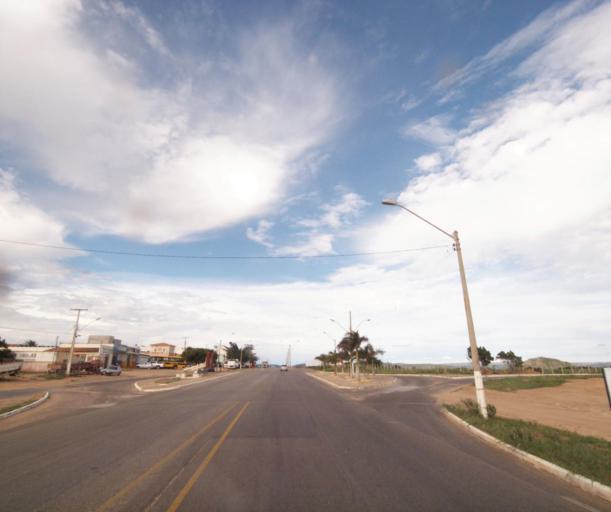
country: BR
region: Bahia
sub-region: Guanambi
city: Guanambi
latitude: -14.2037
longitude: -42.7587
